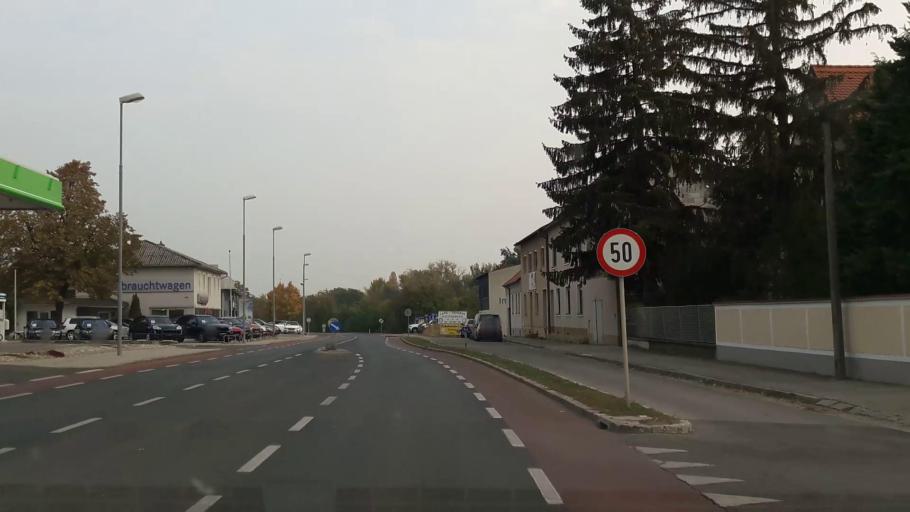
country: AT
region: Burgenland
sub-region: Politischer Bezirk Neusiedl am See
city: Neusiedl am See
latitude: 47.9376
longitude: 16.8549
